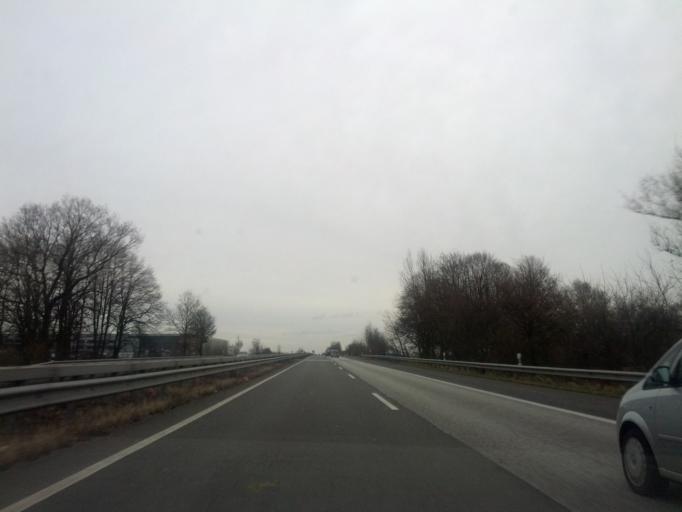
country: DE
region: Lower Saxony
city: Buchholz in der Nordheide
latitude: 53.3725
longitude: 9.9027
